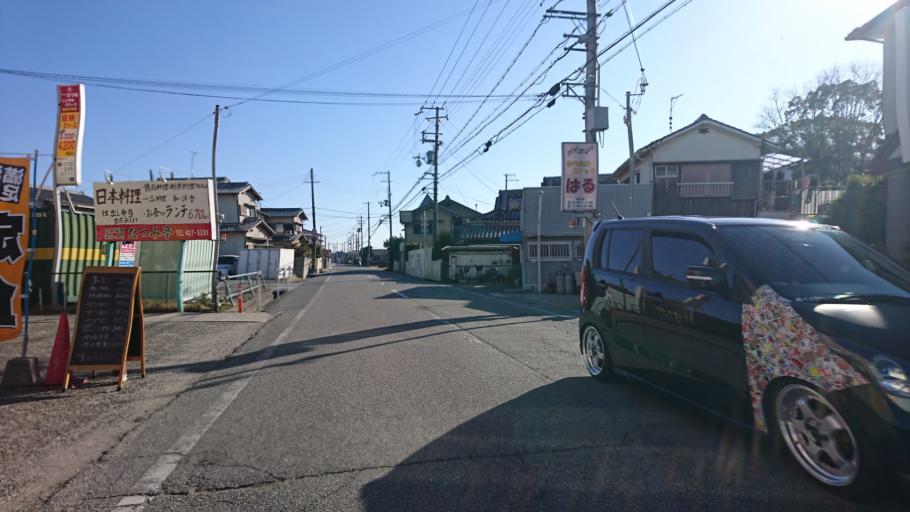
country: JP
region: Hyogo
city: Kakogawacho-honmachi
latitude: 34.7526
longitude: 134.8800
